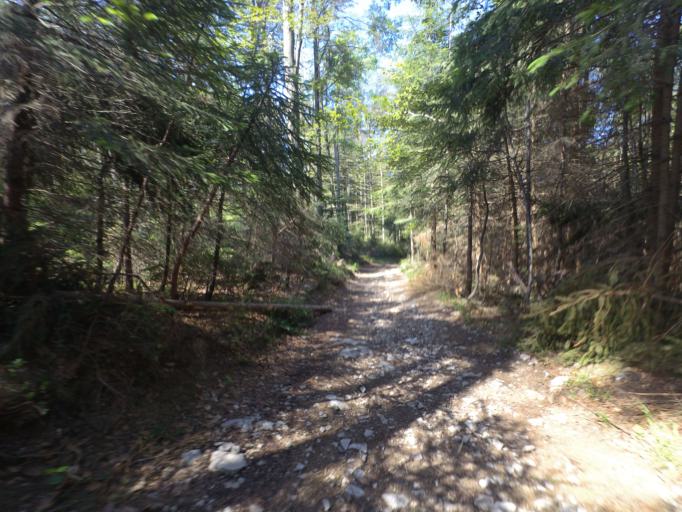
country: AT
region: Salzburg
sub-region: Politischer Bezirk Salzburg-Umgebung
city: Elsbethen
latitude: 47.7526
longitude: 13.1217
